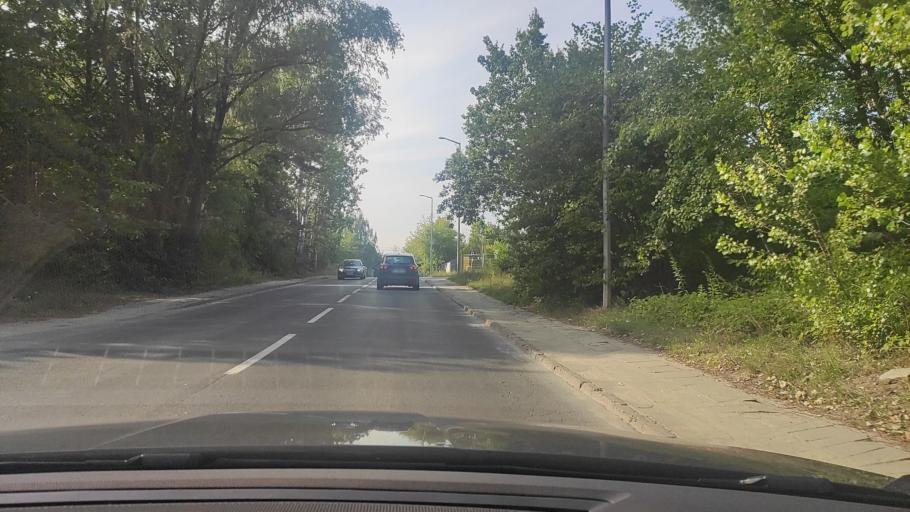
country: PL
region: Greater Poland Voivodeship
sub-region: Powiat poznanski
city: Swarzedz
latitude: 52.3878
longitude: 17.0268
